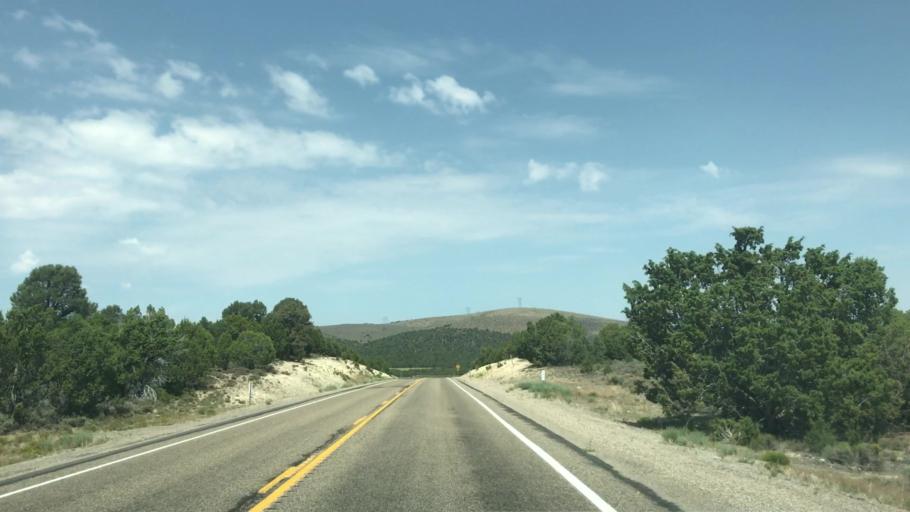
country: US
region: Nevada
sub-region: White Pine County
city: Ely
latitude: 39.3890
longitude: -115.0774
